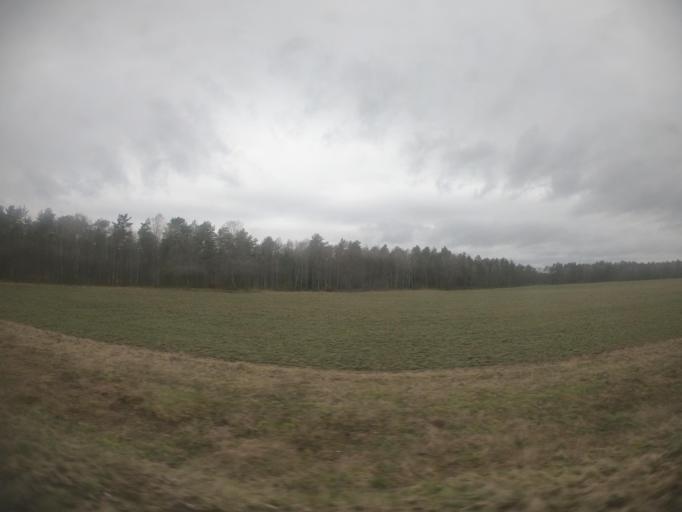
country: PL
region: West Pomeranian Voivodeship
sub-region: Powiat szczecinecki
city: Bialy Bor
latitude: 53.8221
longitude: 16.8705
